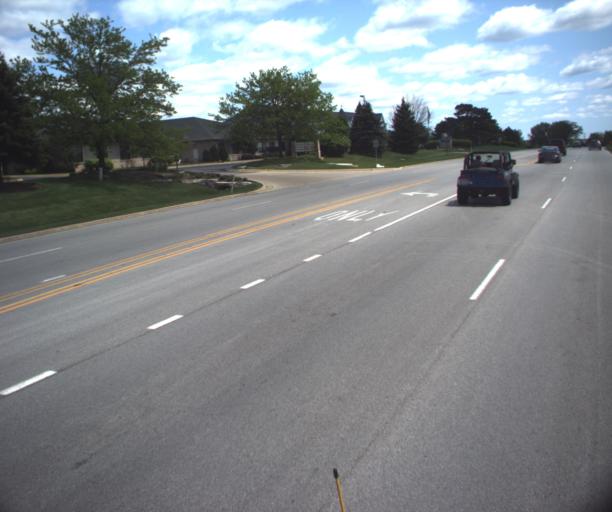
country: US
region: Illinois
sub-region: Kane County
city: Geneva
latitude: 41.8689
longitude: -88.2779
